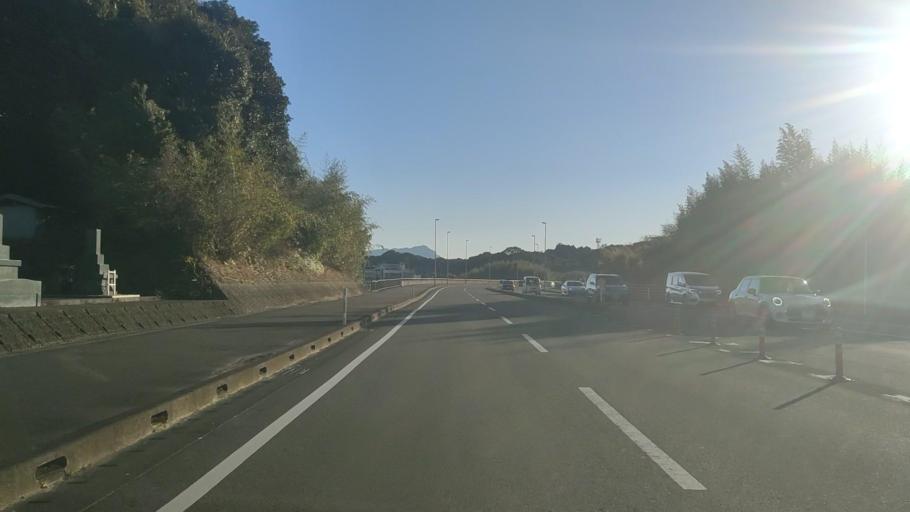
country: JP
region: Miyazaki
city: Miyazaki-shi
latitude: 31.8888
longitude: 131.4029
